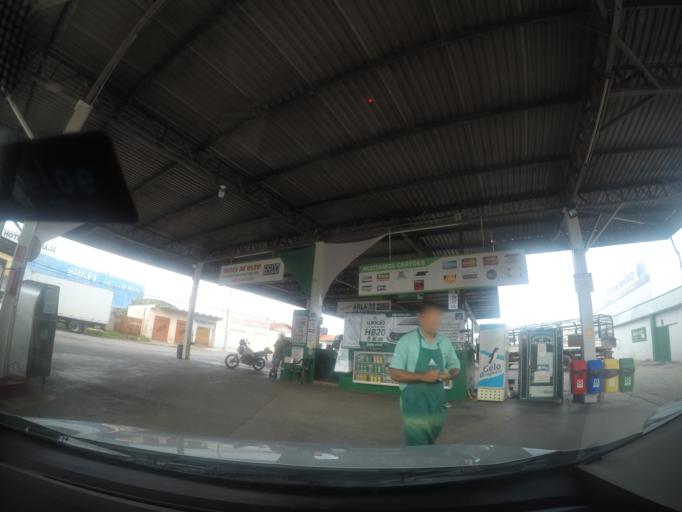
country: BR
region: Goias
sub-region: Goiania
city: Goiania
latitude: -16.6734
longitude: -49.3061
